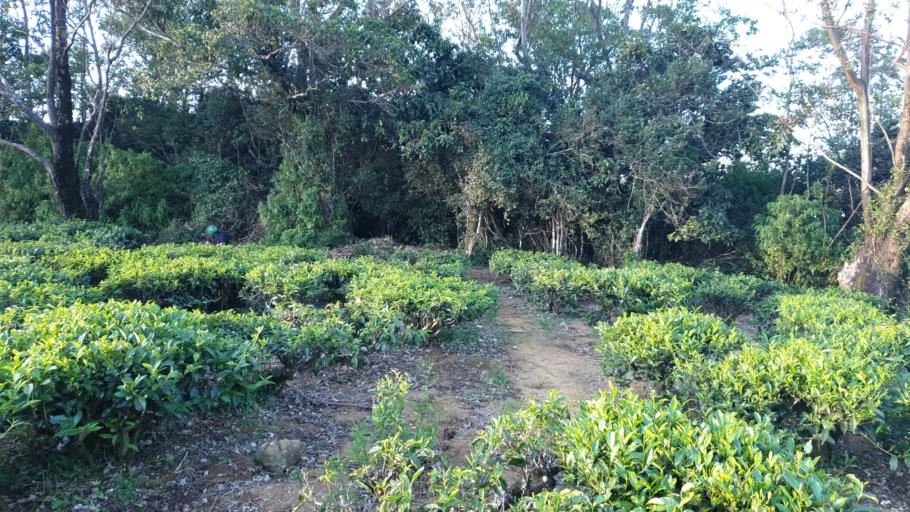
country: LK
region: Central
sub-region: Nuwara Eliya District
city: Nuwara Eliya
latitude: 6.9606
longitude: 80.7615
